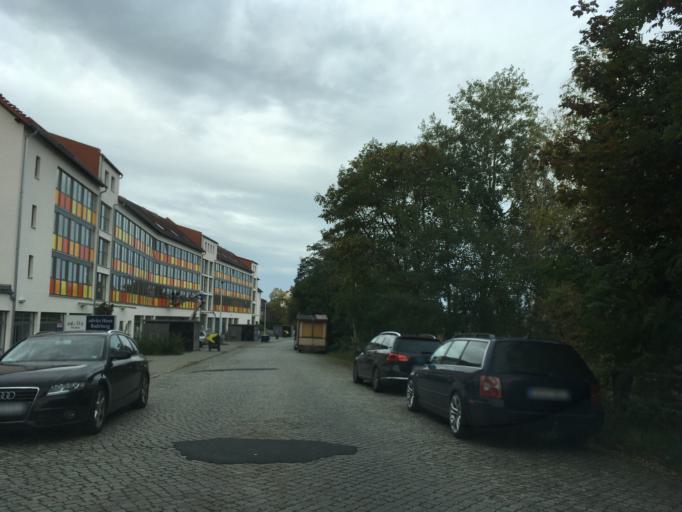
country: DE
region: Saxony
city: Radeberg
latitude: 51.1100
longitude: 13.9177
